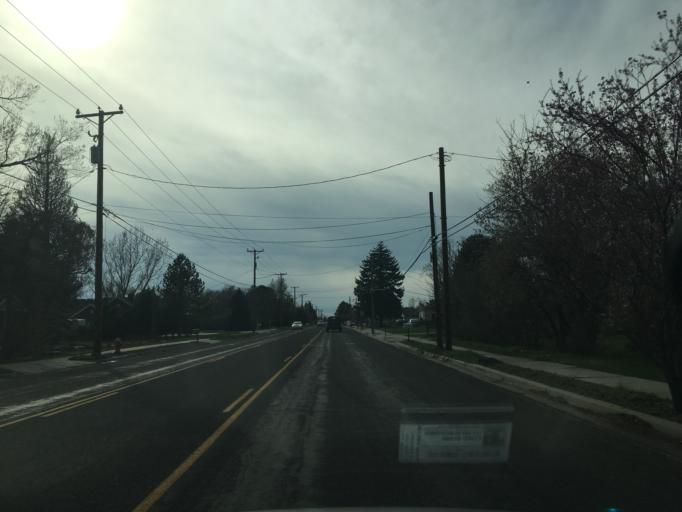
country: US
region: Utah
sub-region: Davis County
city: Layton
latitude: 41.0602
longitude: -111.9795
